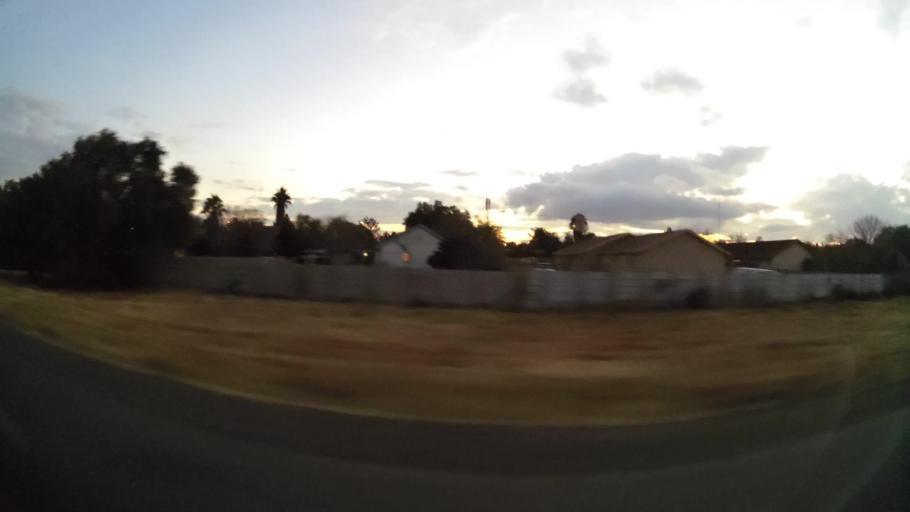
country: ZA
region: Orange Free State
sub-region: Mangaung Metropolitan Municipality
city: Bloemfontein
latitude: -29.1637
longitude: 26.1800
